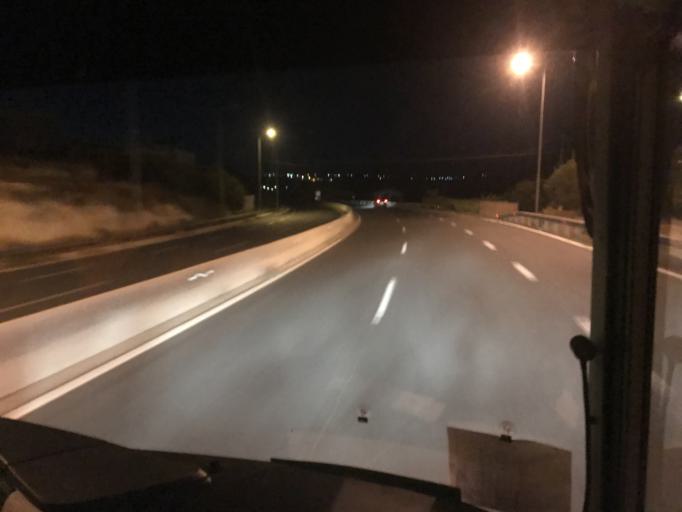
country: GR
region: Crete
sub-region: Nomos Irakleiou
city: Skalanion
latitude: 35.2660
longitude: 25.1845
